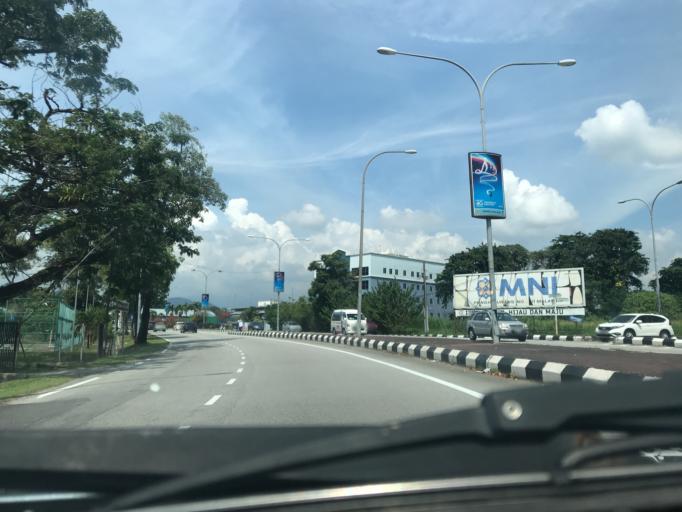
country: MY
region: Perak
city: Ipoh
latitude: 4.6018
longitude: 101.0978
